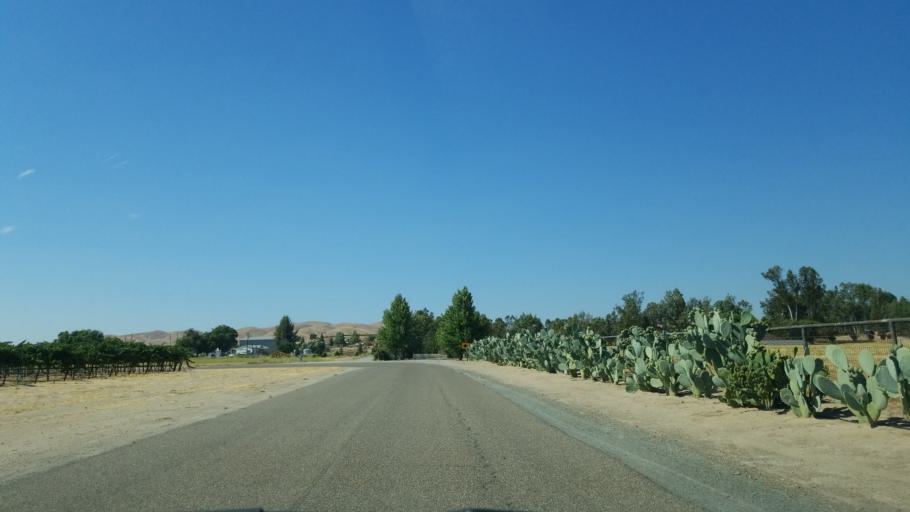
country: US
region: California
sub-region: San Luis Obispo County
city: San Miguel
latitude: 35.7207
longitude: -120.6495
